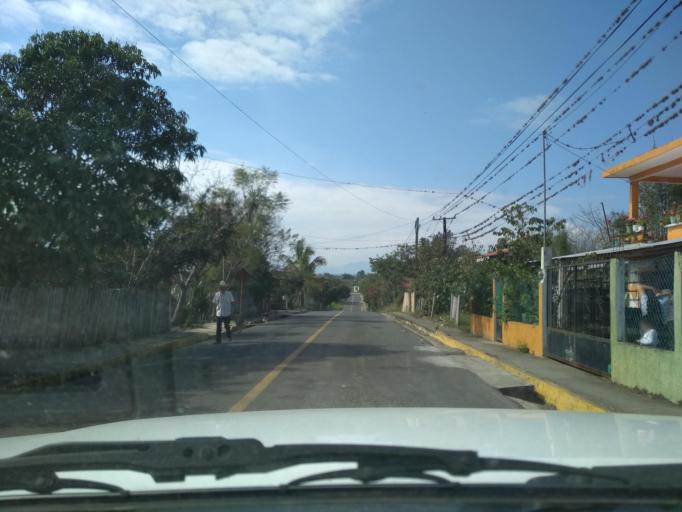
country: MX
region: Veracruz
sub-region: Coatepec
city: Tuzamapan
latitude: 19.3676
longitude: -96.8927
